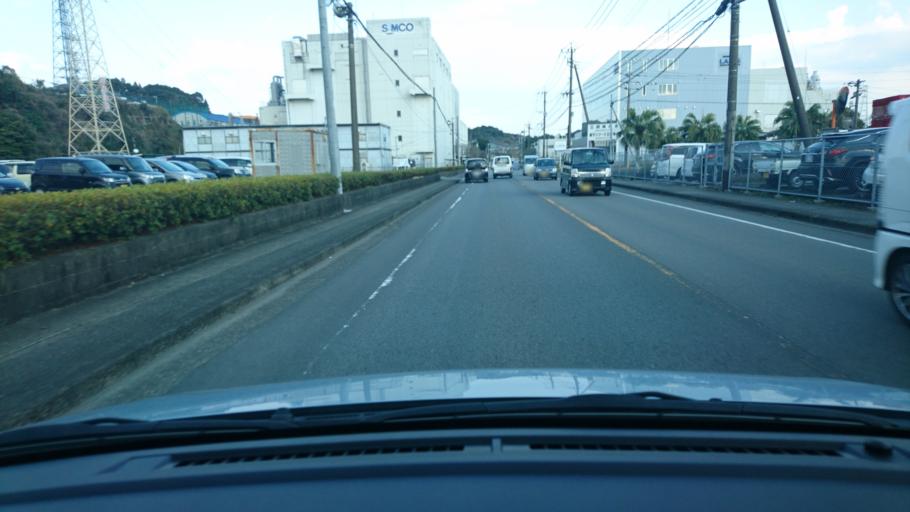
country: JP
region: Miyazaki
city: Miyazaki-shi
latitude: 31.8554
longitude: 131.4035
